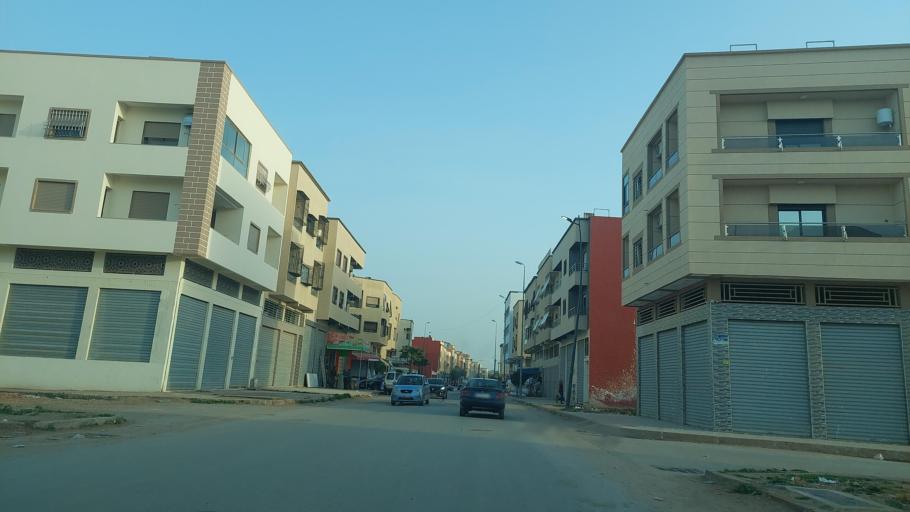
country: MA
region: Grand Casablanca
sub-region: Mediouna
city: Mediouna
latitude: 33.3800
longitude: -7.5335
